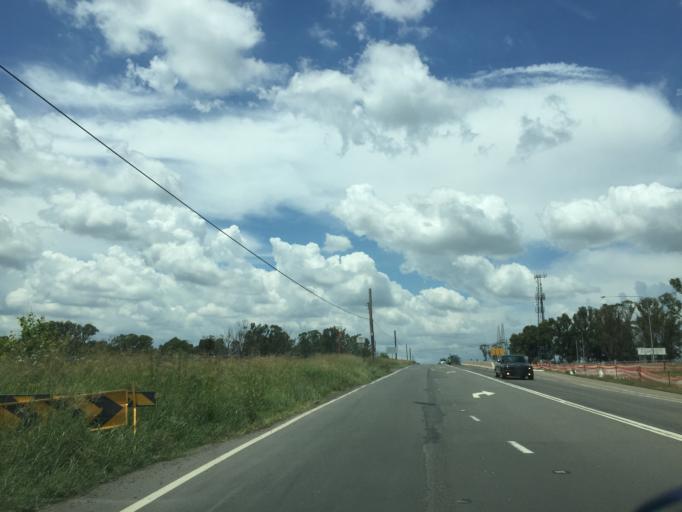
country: AU
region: New South Wales
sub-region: Blacktown
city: Hassall Grove
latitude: -33.7106
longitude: 150.8412
